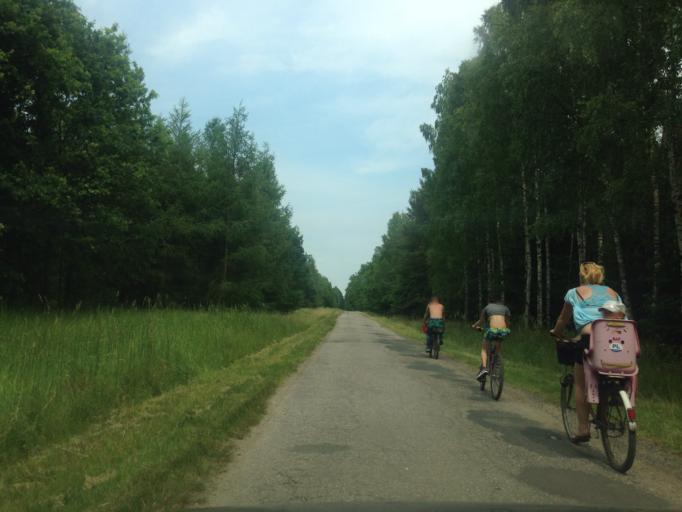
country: PL
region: Kujawsko-Pomorskie
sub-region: Powiat golubsko-dobrzynski
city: Radomin
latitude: 53.1496
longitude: 19.1379
